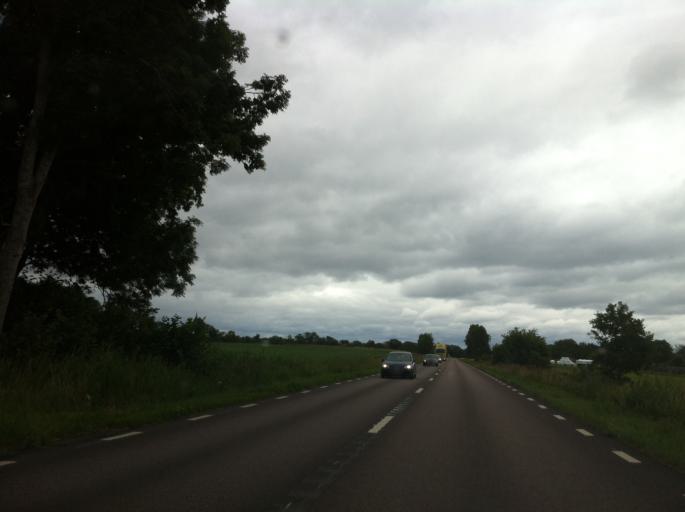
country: SE
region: Kalmar
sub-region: Borgholms Kommun
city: Borgholm
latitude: 57.1399
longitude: 16.9949
